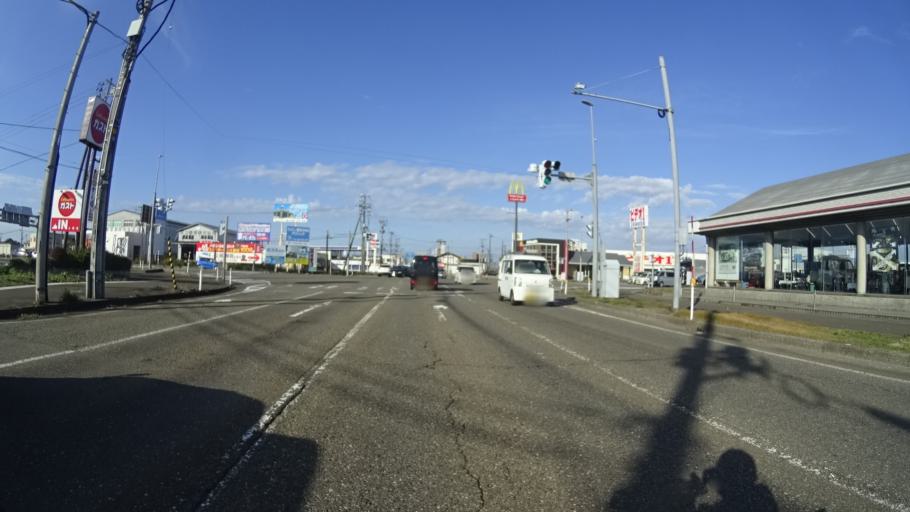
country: JP
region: Niigata
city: Joetsu
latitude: 37.1609
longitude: 138.2374
